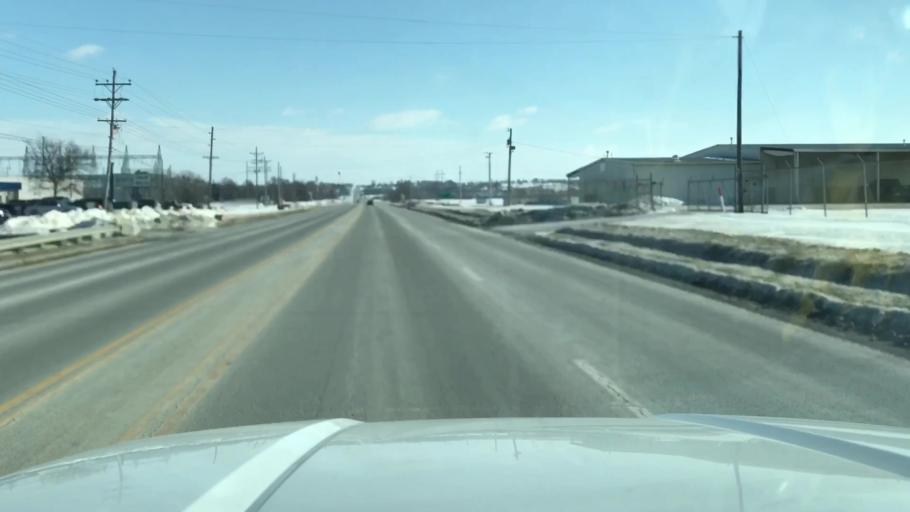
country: US
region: Missouri
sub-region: Nodaway County
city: Maryville
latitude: 40.3452
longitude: -94.8474
